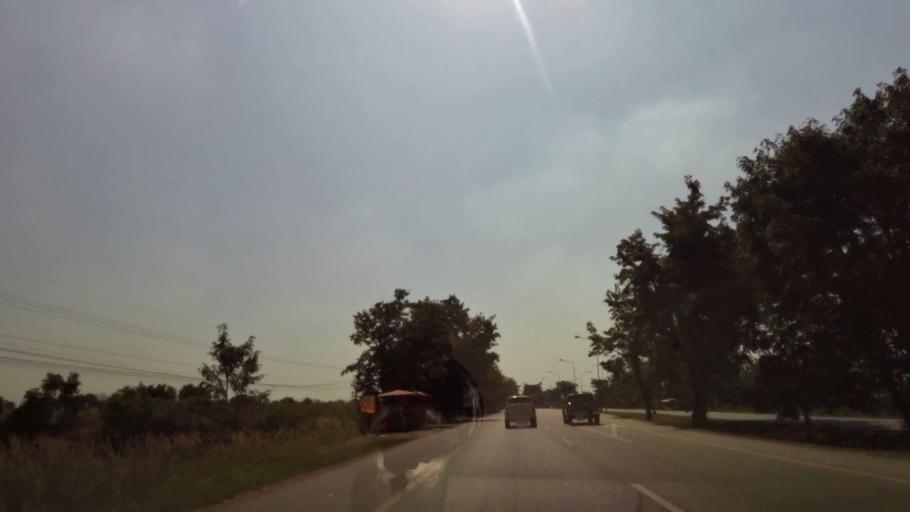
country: TH
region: Phichit
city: Wachira Barami
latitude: 16.4087
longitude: 100.1426
